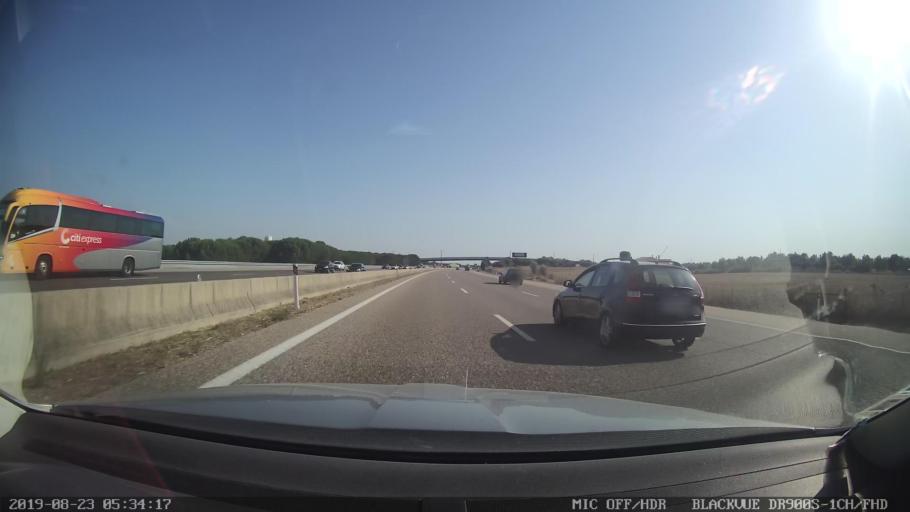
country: PT
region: Santarem
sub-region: Alcanena
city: Alcanena
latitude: 39.4047
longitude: -8.6370
